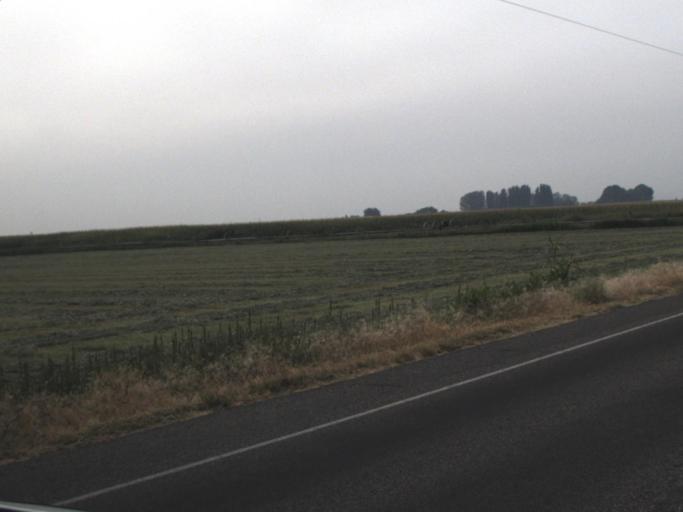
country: US
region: Washington
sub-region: Yakima County
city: Sunnyside
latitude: 46.3022
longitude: -119.9872
